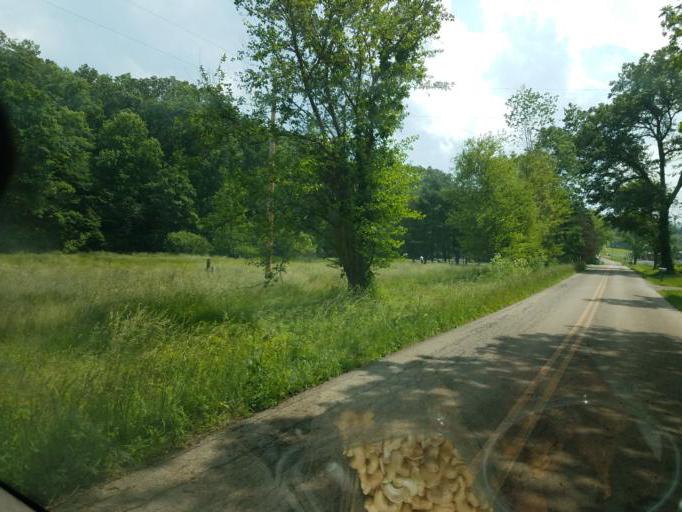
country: US
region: Ohio
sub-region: Knox County
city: Oak Hill
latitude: 40.3787
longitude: -82.2672
